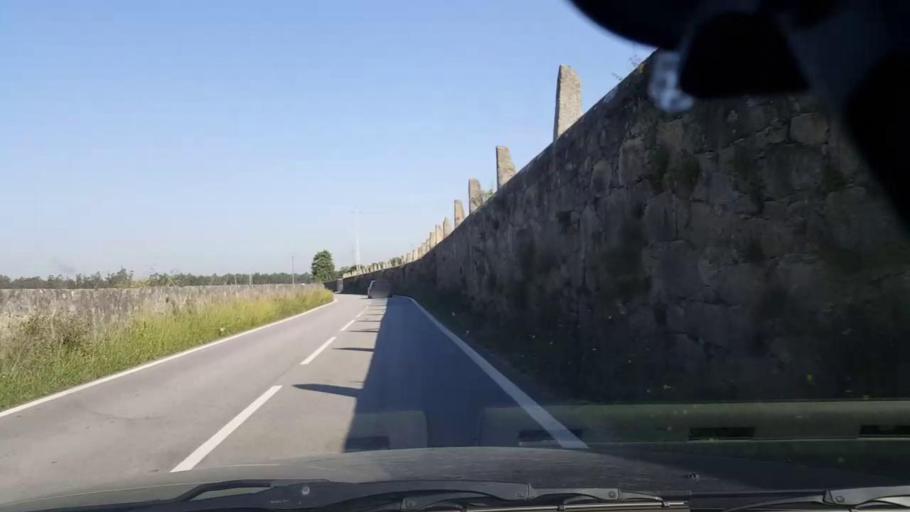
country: PT
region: Porto
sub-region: Vila do Conde
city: Arvore
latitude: 41.3217
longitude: -8.6802
